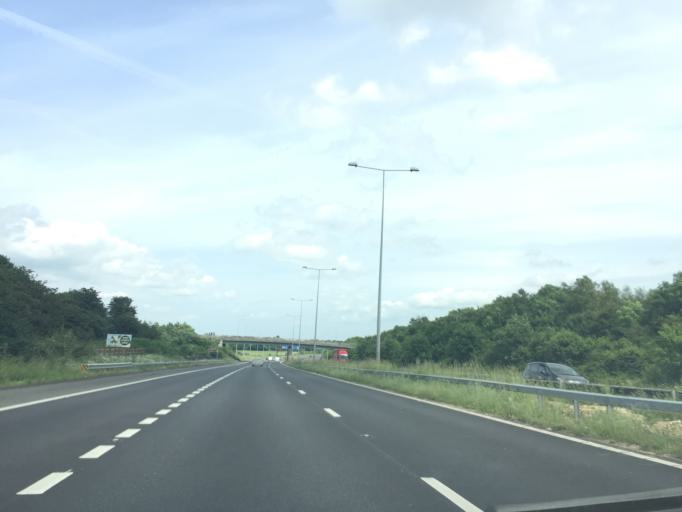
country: GB
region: England
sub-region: Kent
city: Boxley
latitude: 51.3303
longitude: 0.5692
